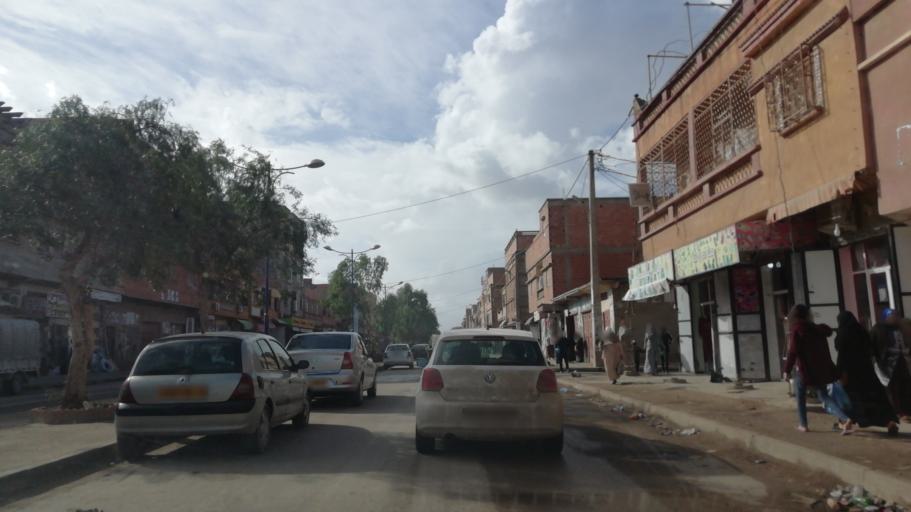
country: DZ
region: Oran
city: Es Senia
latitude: 35.6441
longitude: -0.5724
